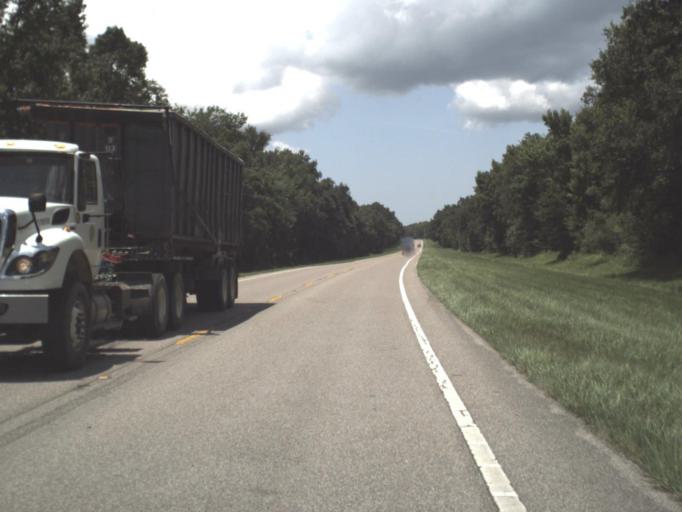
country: US
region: Florida
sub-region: Hernando County
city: North Brooksville
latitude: 28.6451
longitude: -82.4387
